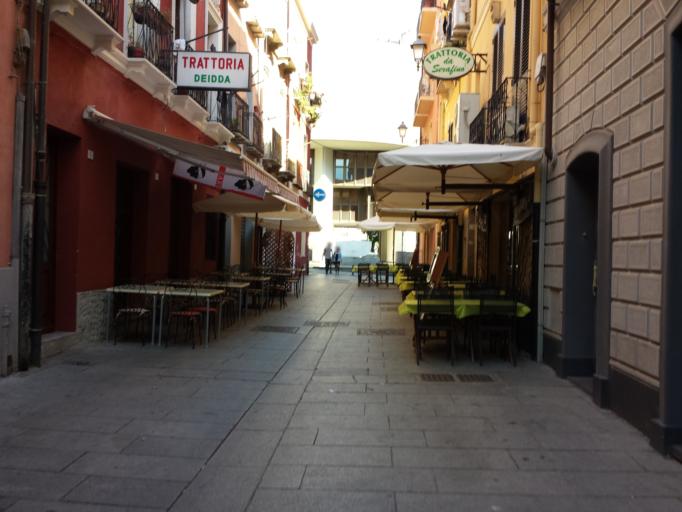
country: IT
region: Sardinia
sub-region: Provincia di Cagliari
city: Cagliari
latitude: 39.2138
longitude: 9.1140
